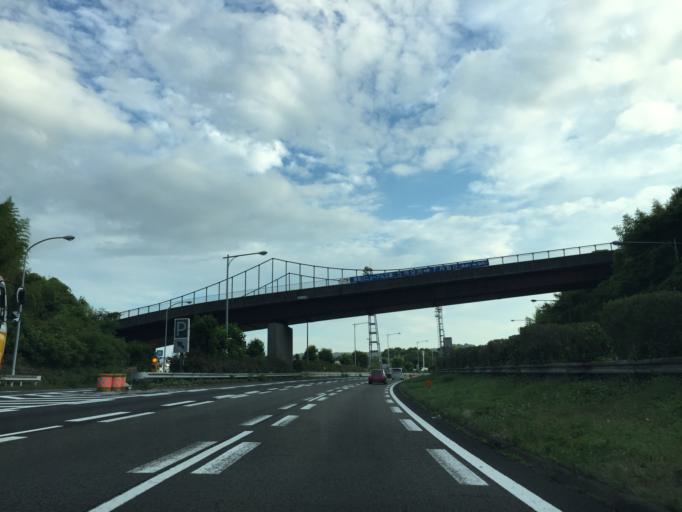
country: JP
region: Kanagawa
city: Hadano
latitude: 35.3452
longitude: 139.2040
